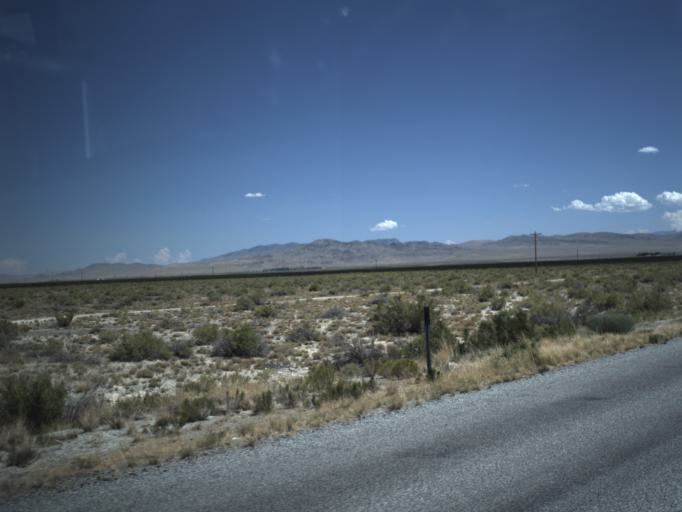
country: US
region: Nevada
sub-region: White Pine County
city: McGill
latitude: 39.0566
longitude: -114.0424
